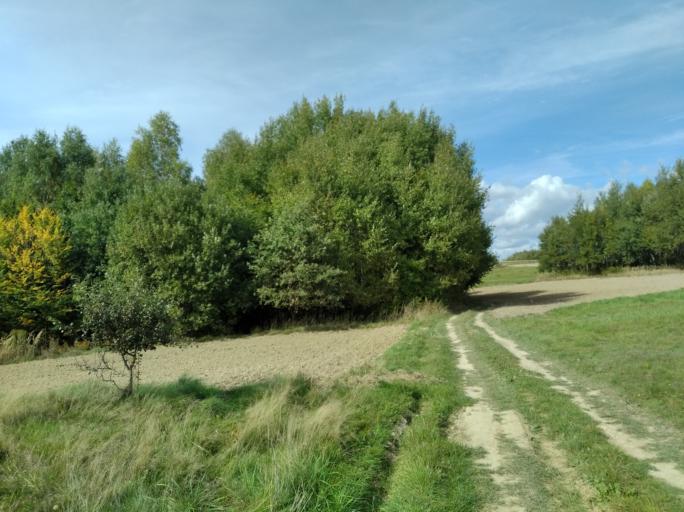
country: PL
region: Subcarpathian Voivodeship
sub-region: Powiat strzyzowski
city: Jawornik
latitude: 49.8431
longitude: 21.8655
